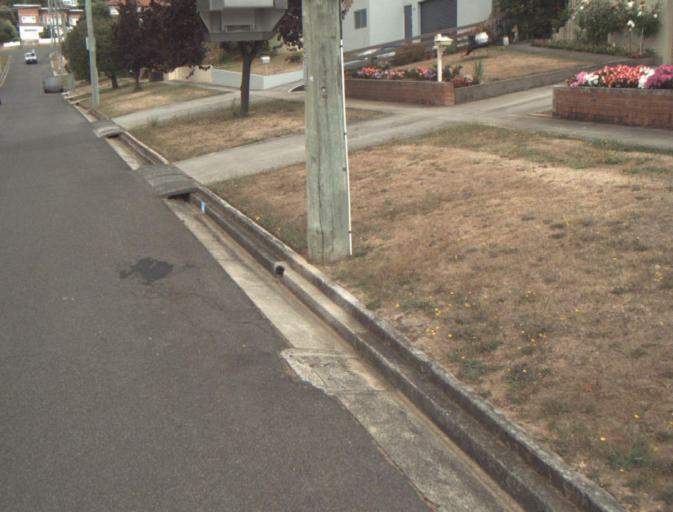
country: AU
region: Tasmania
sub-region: Launceston
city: Summerhill
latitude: -41.4686
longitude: 147.1537
